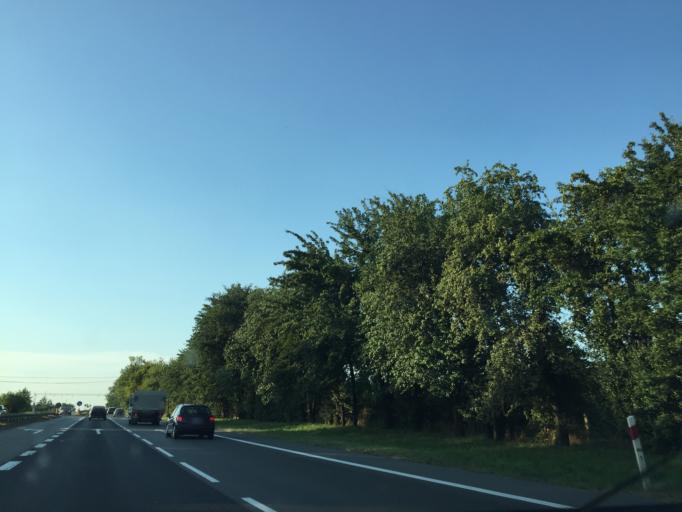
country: PL
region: Masovian Voivodeship
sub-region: Powiat piaseczynski
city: Tarczyn
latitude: 51.9651
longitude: 20.8369
